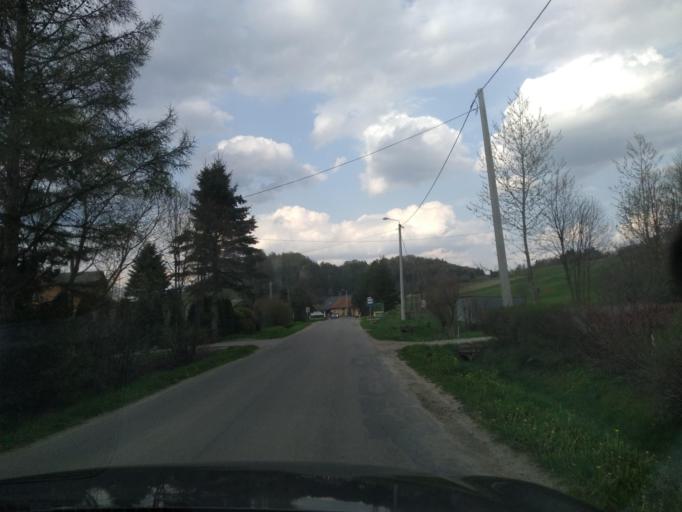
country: PL
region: Subcarpathian Voivodeship
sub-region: Powiat sanocki
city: Czaszyn
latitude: 49.4349
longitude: 22.2478
